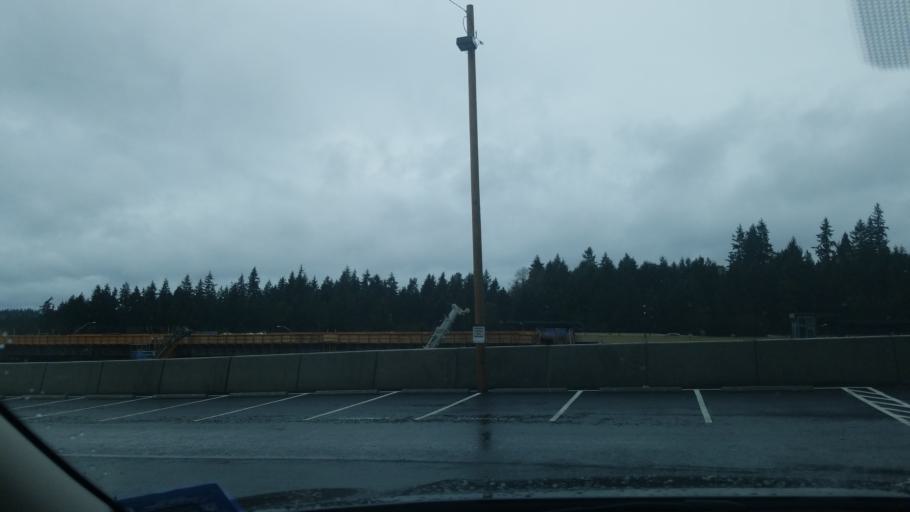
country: US
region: Washington
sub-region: Snohomish County
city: Mountlake Terrace
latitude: 47.7857
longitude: -122.3134
